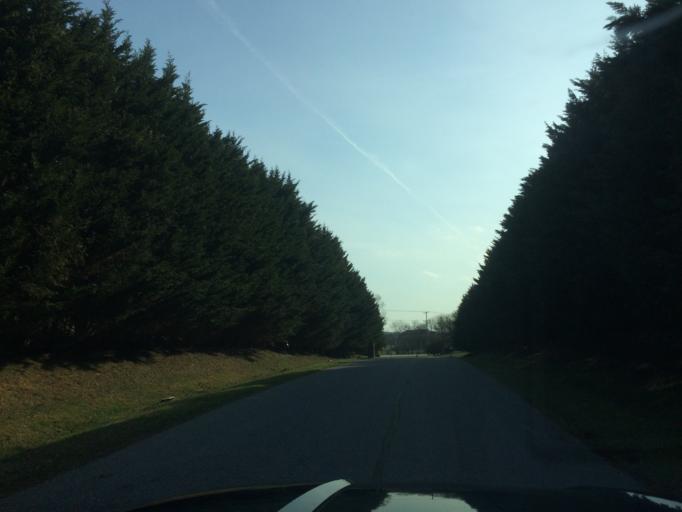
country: US
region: Maryland
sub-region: Howard County
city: Highland
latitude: 39.2073
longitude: -76.9471
